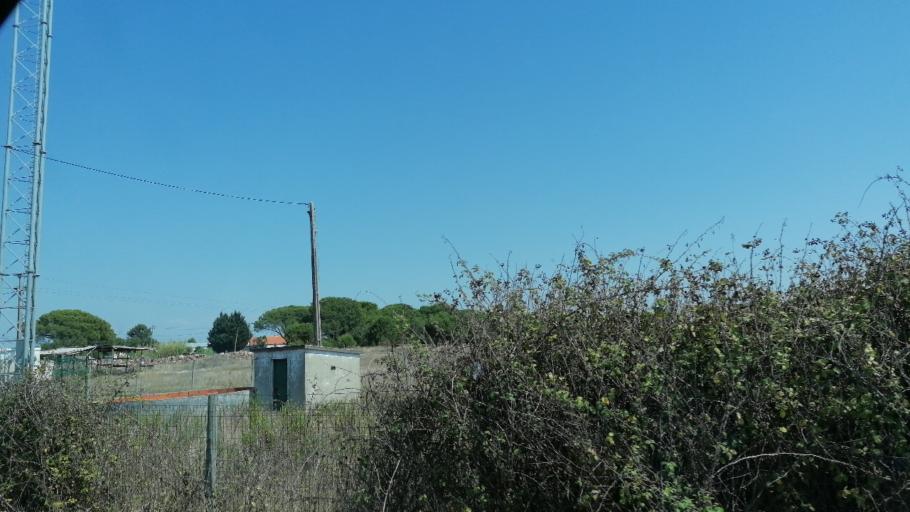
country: PT
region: Santarem
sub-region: Benavente
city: Poceirao
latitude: 38.7482
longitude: -8.6675
